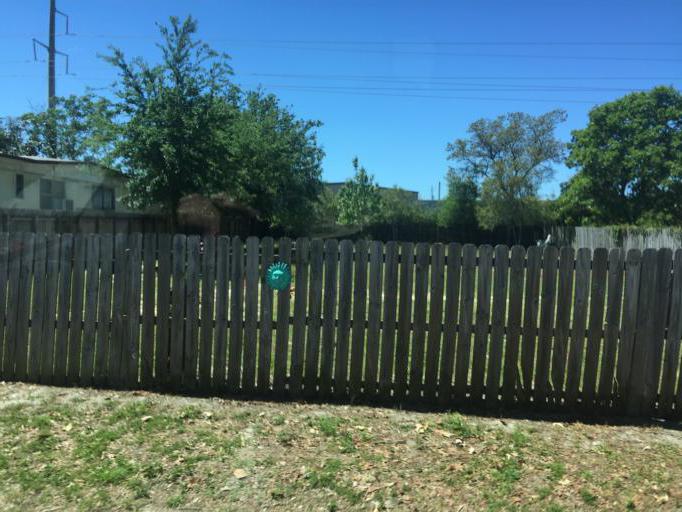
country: US
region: Florida
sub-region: Bay County
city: Laguna Beach
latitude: 30.2549
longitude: -85.9386
